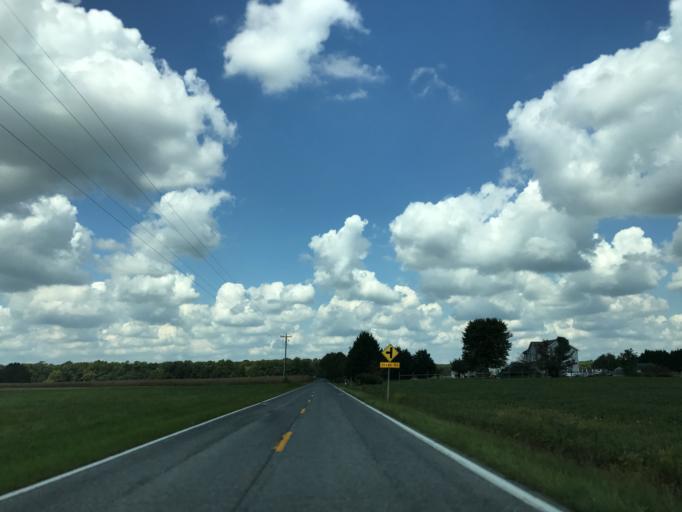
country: US
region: Maryland
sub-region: Caroline County
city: Ridgely
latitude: 39.0468
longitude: -75.9177
